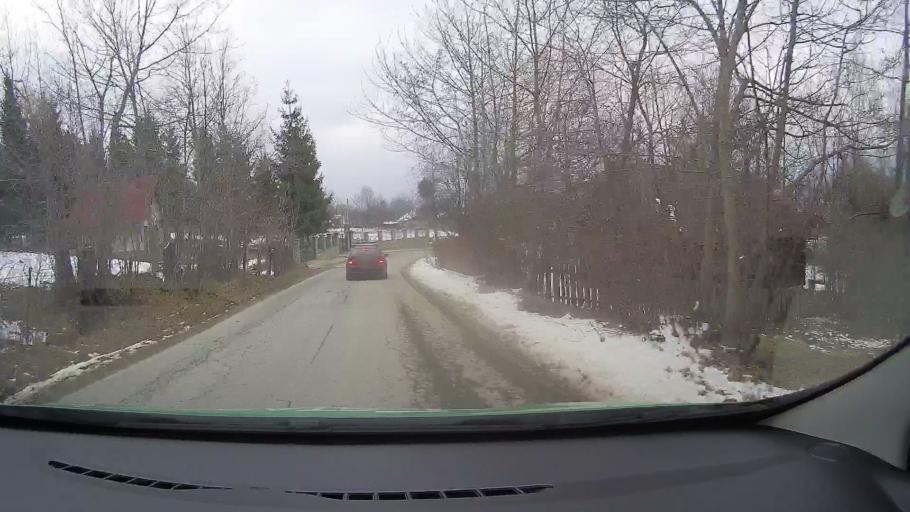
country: RO
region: Brasov
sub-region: Comuna Bran
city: Bran
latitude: 45.5327
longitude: 25.3443
